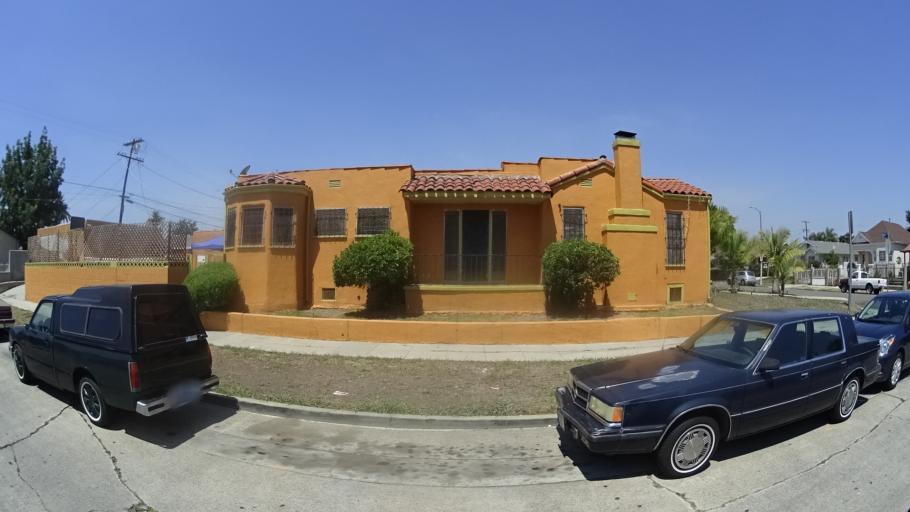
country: US
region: California
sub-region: Los Angeles County
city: Westmont
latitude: 33.9734
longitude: -118.2962
